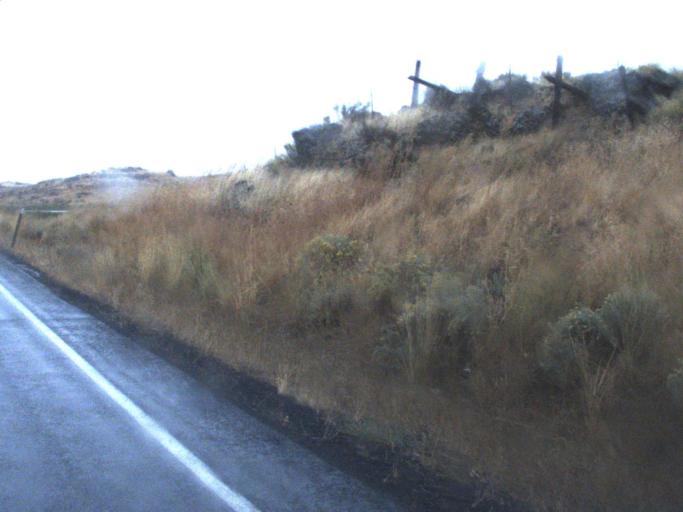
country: US
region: Washington
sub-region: Spokane County
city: Medical Lake
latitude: 47.2703
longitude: -117.9438
